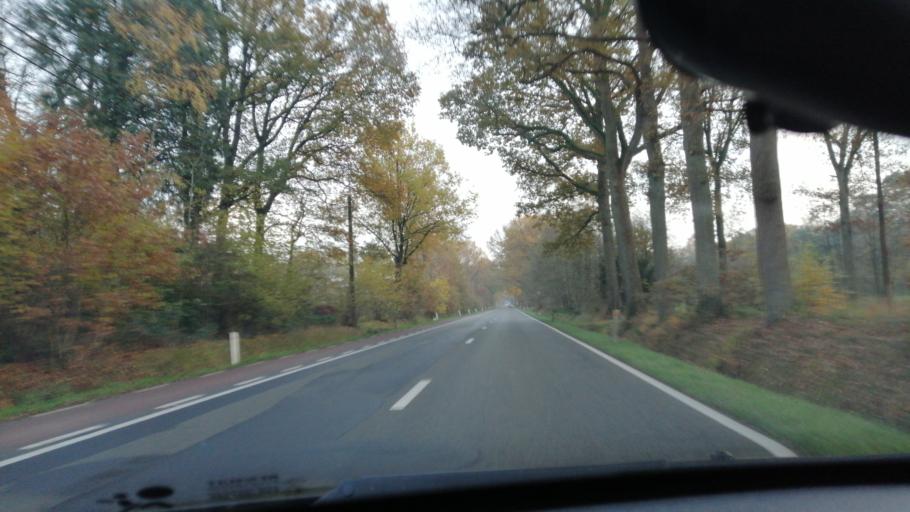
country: BE
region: Flanders
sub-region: Provincie Antwerpen
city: Oostmalle
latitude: 51.2871
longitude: 4.7530
